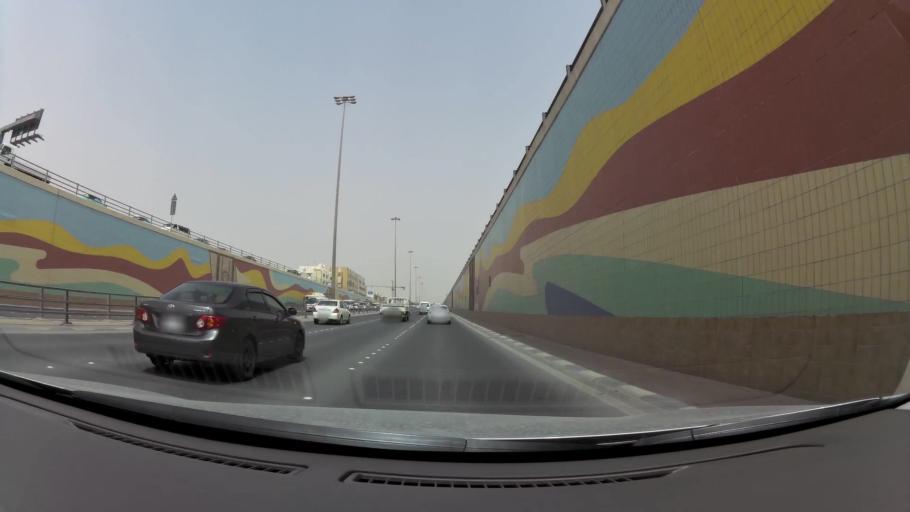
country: QA
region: Baladiyat ad Dawhah
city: Doha
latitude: 25.2651
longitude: 51.4964
